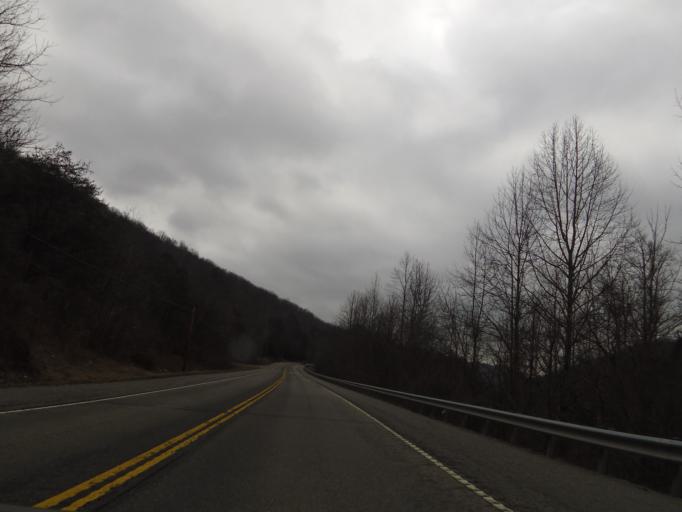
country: US
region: Tennessee
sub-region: Campbell County
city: Caryville
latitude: 36.4038
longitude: -84.2878
